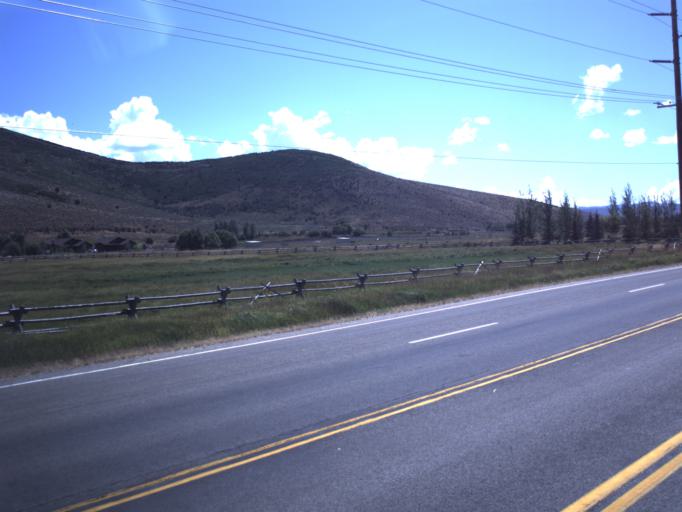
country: US
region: Utah
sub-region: Summit County
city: Kamas
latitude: 40.6598
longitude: -111.2808
